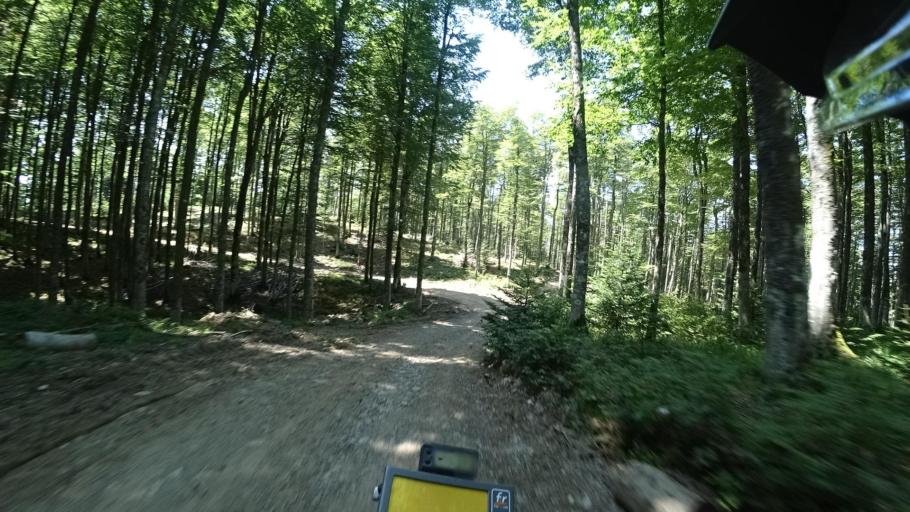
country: HR
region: Primorsko-Goranska
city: Vrbovsko
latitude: 45.2678
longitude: 14.9312
